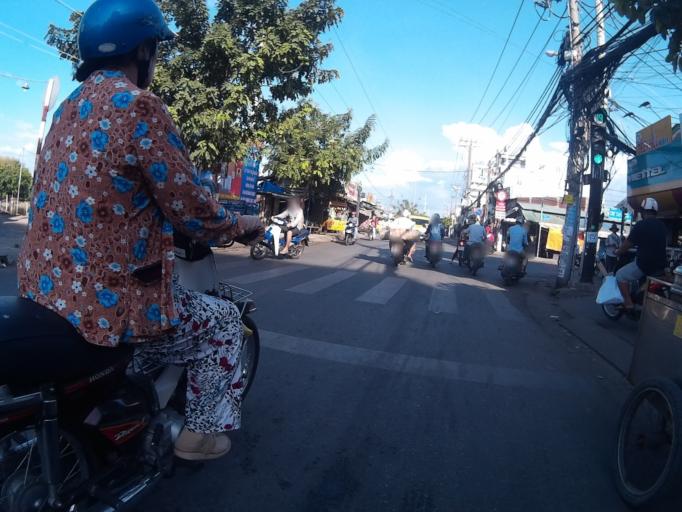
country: VN
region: Ho Chi Minh City
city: Quan Bon
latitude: 10.7517
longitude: 106.7049
